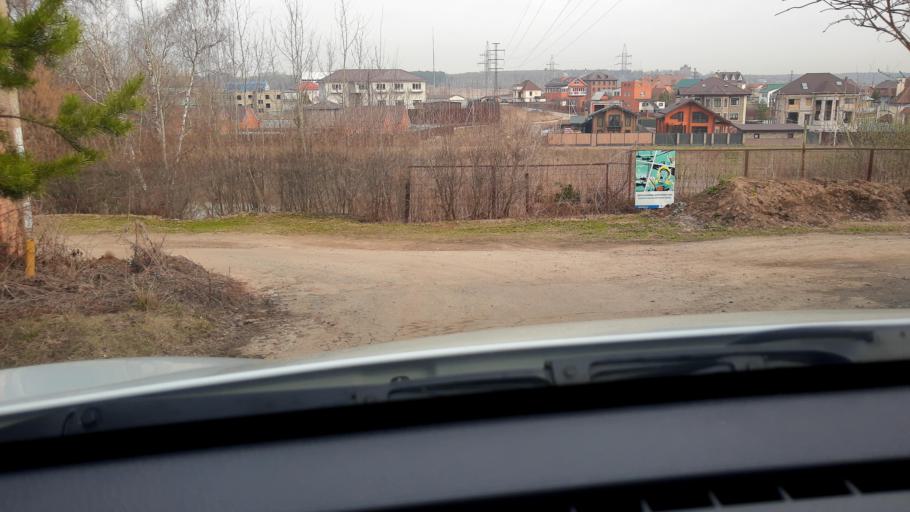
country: RU
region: Moskovskaya
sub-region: Leninskiy Rayon
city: Molokovo
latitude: 55.4928
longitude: 37.8522
